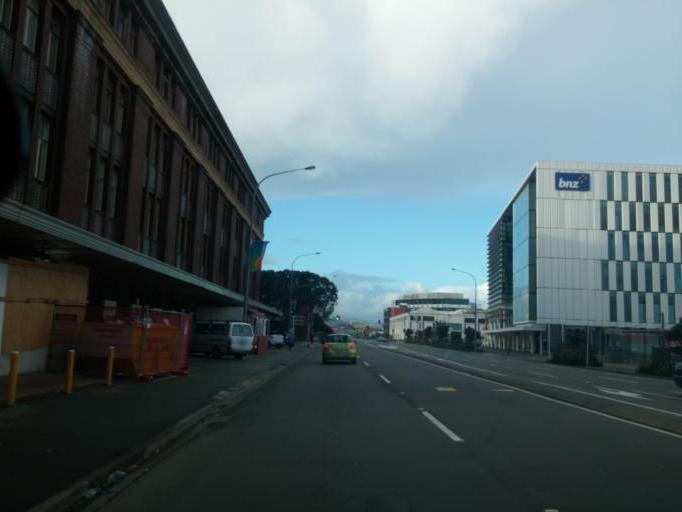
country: NZ
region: Wellington
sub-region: Wellington City
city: Wellington
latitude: -41.2798
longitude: 174.7807
